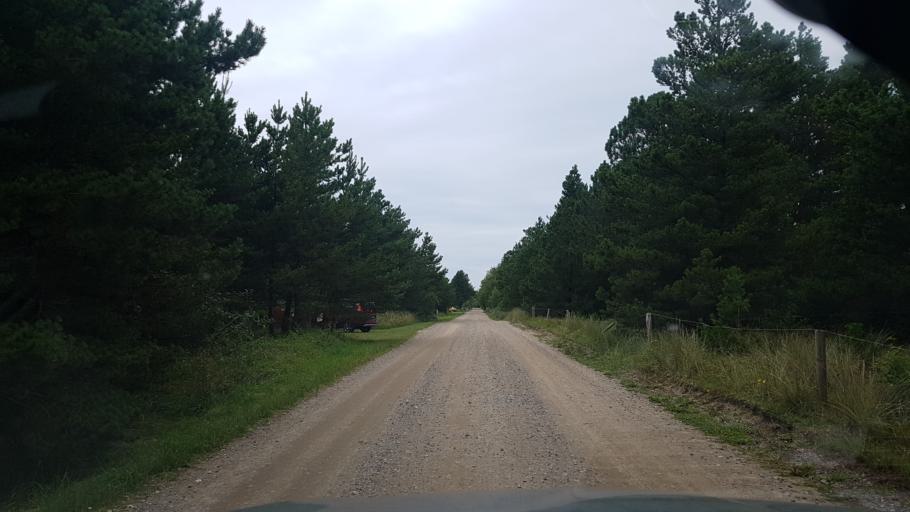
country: DE
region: Schleswig-Holstein
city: List
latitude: 55.0867
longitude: 8.5360
